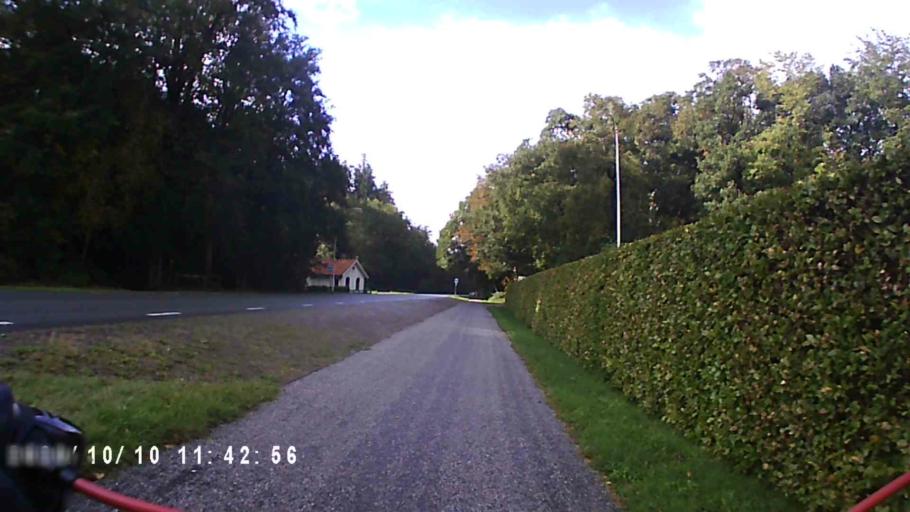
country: NL
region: Friesland
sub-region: Gemeente Smallingerland
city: Drachten
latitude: 53.0612
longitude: 6.0958
